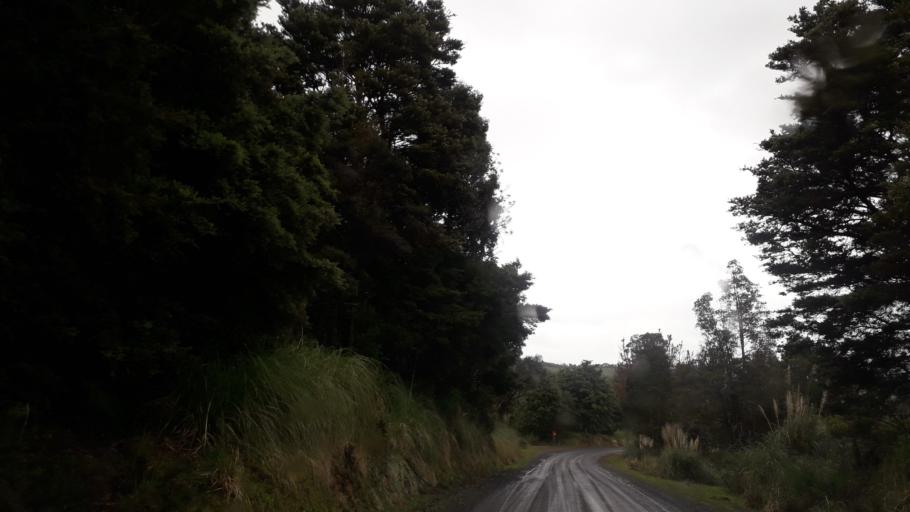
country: NZ
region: Northland
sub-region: Far North District
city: Kaitaia
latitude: -35.3738
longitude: 173.4120
